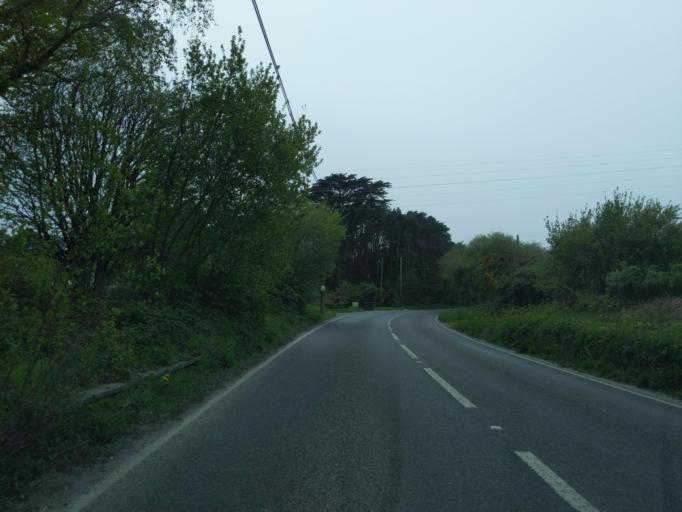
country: GB
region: England
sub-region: Cornwall
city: Par
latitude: 50.3432
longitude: -4.7114
